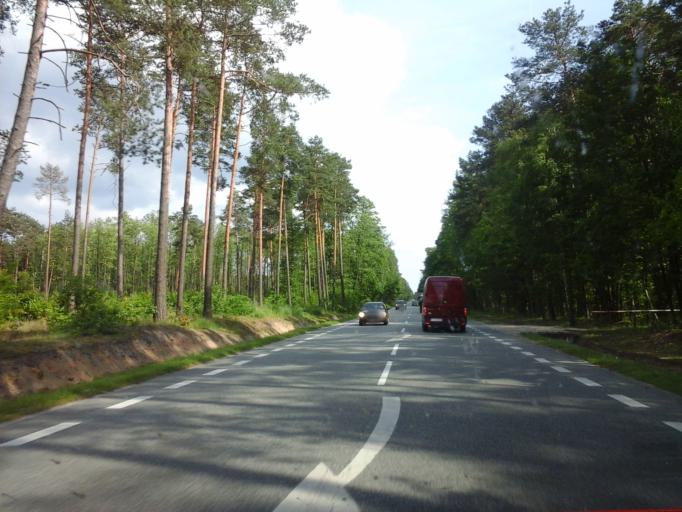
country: PL
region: Swietokrzyskie
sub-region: Powiat konecki
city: Ruda Maleniecka
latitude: 51.1635
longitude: 20.2261
